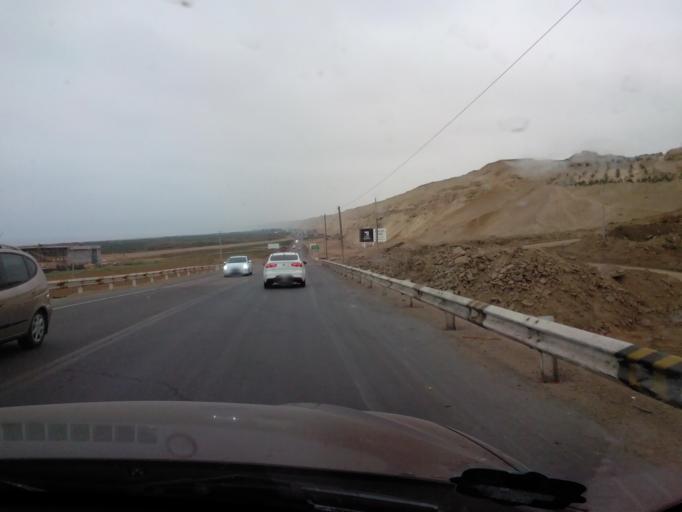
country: PE
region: Ica
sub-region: Provincia de Chincha
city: Sunampe
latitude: -13.4124
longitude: -76.1894
